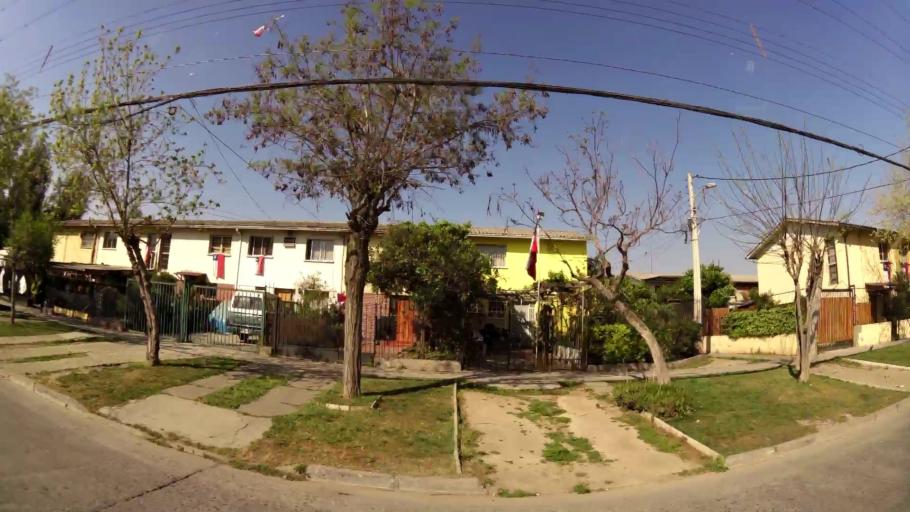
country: CL
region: Santiago Metropolitan
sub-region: Provincia de Santiago
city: Santiago
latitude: -33.4678
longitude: -70.6219
